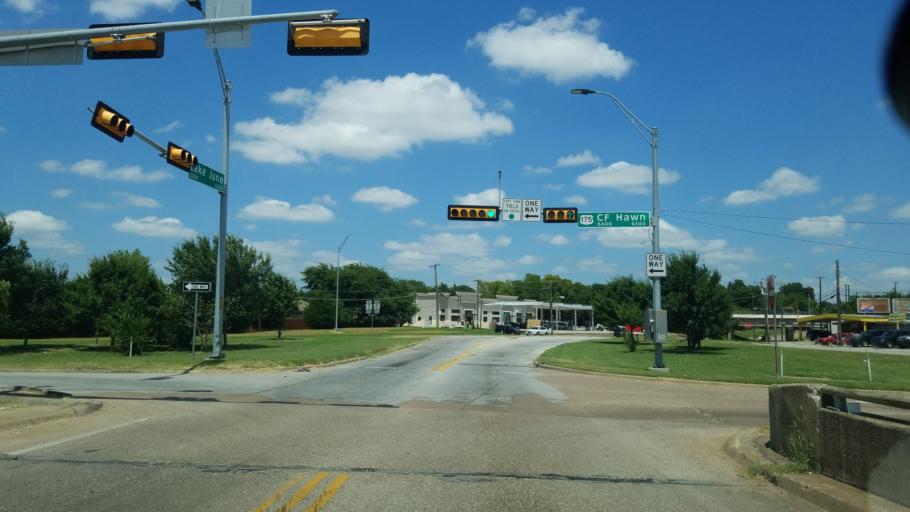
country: US
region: Texas
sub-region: Dallas County
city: Hutchins
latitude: 32.7339
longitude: -96.7128
